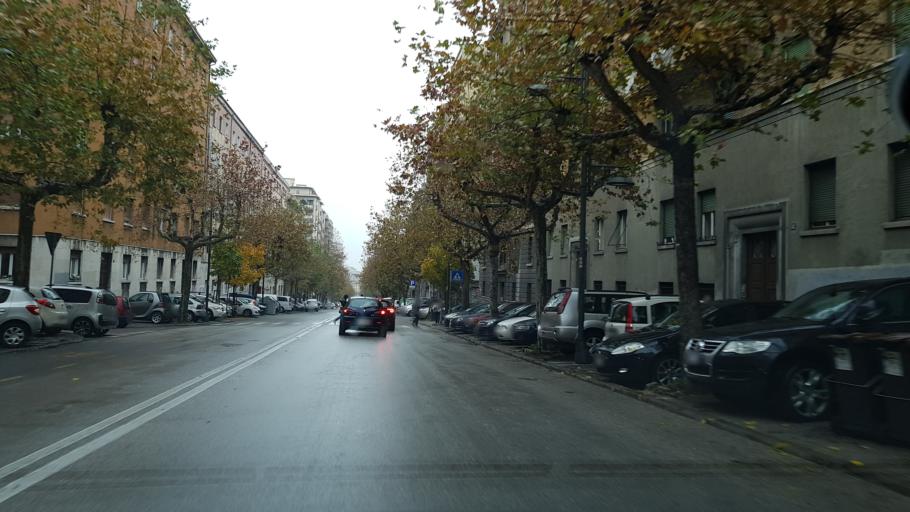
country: IT
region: Friuli Venezia Giulia
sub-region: Provincia di Trieste
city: Trieste
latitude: 45.6410
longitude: 13.7869
